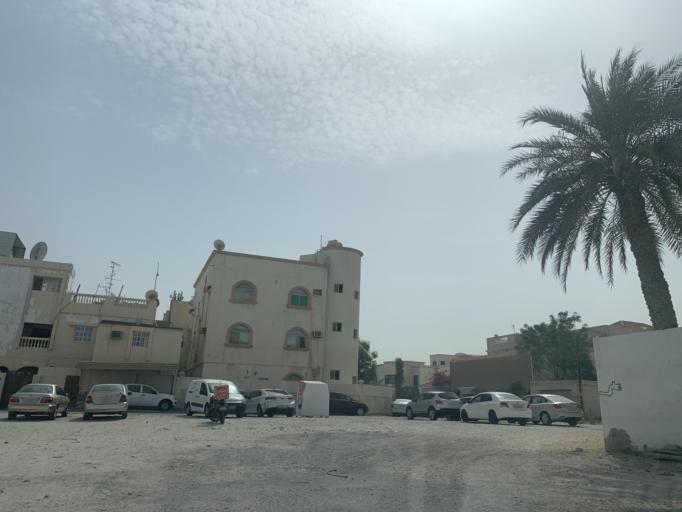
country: BH
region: Northern
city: Ar Rifa'
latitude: 26.1320
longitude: 50.5678
